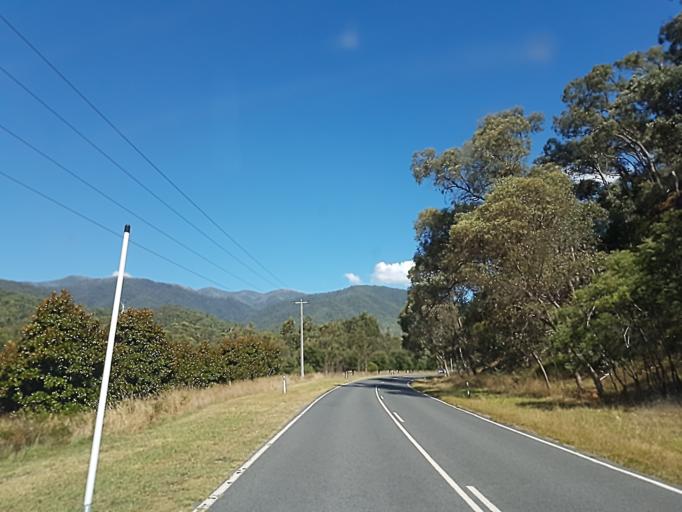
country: AU
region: Victoria
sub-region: Alpine
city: Mount Beauty
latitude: -36.8393
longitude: 147.0781
